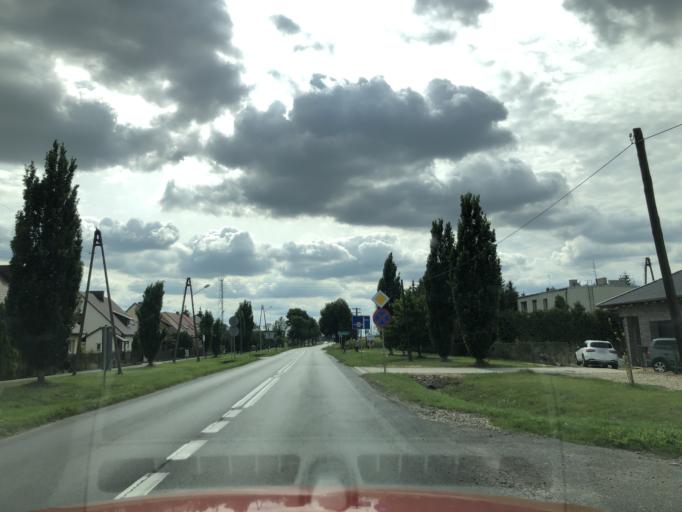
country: PL
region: Greater Poland Voivodeship
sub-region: Powiat szamotulski
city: Pniewy
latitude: 52.5046
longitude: 16.2484
